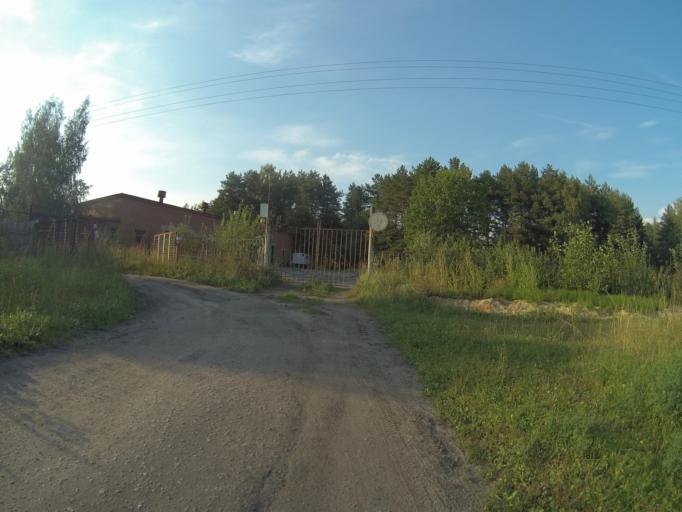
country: RU
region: Vladimir
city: Kommunar
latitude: 56.0651
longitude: 40.4417
